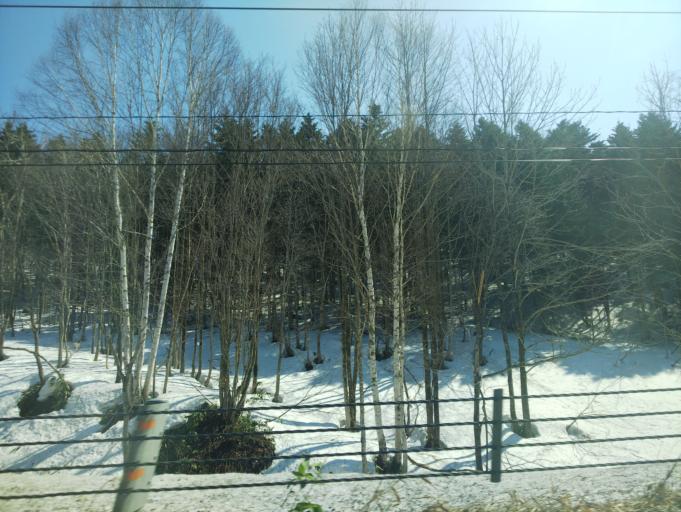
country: JP
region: Hokkaido
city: Nayoro
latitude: 44.7095
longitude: 142.2750
